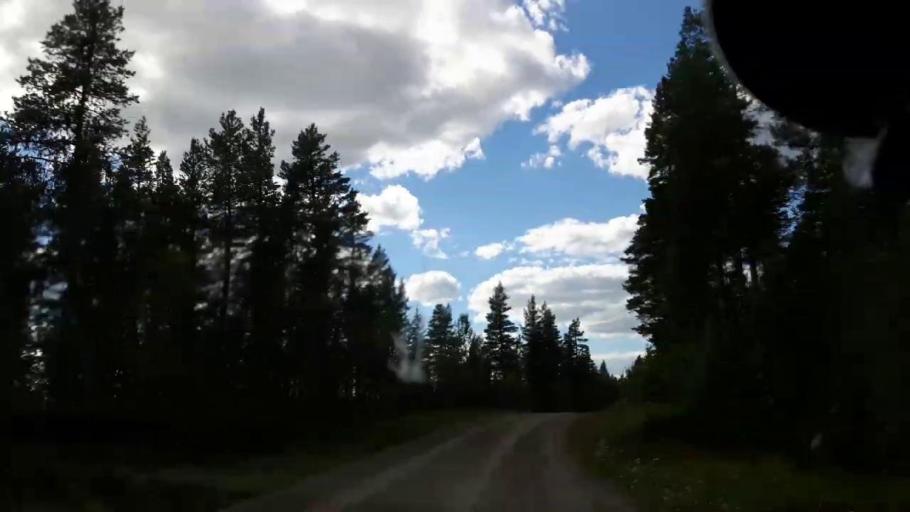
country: SE
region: Vaesternorrland
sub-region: Ange Kommun
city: Ange
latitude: 62.7678
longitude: 15.8564
